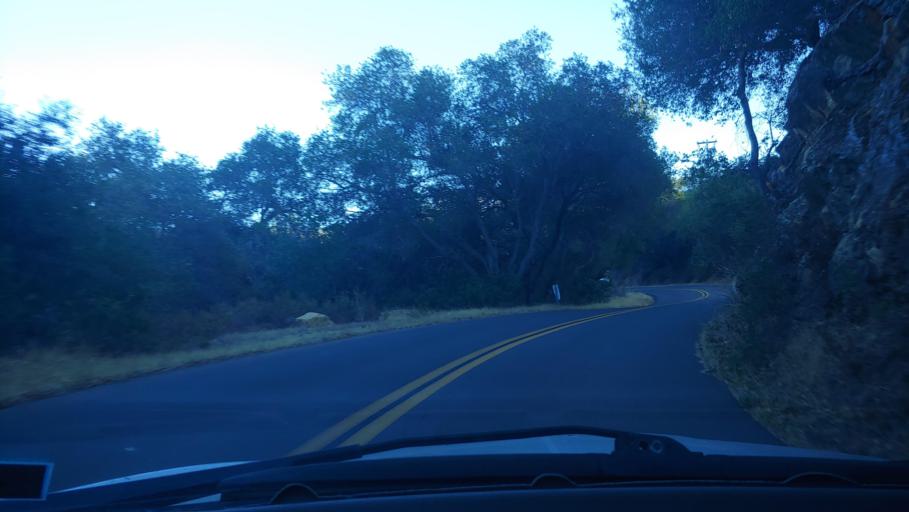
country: US
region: California
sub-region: Santa Barbara County
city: Goleta
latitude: 34.5341
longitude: -119.8425
